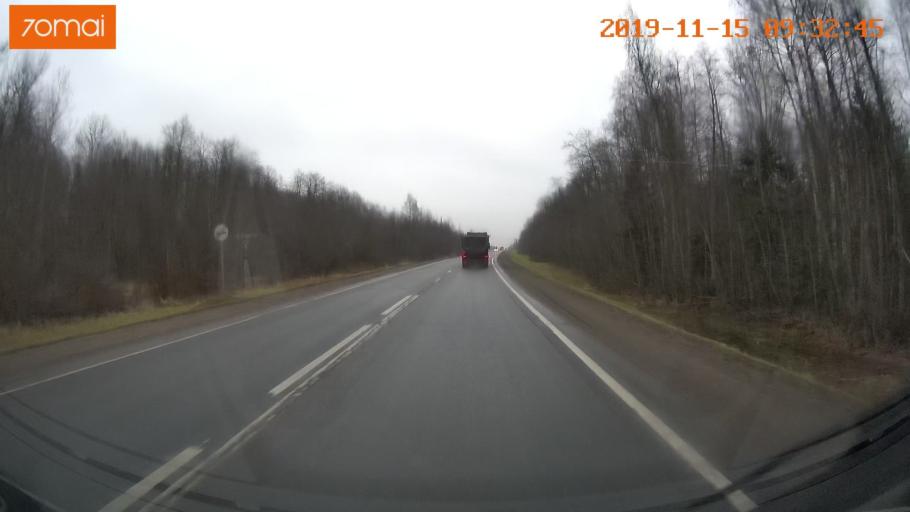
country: RU
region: Vologda
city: Sheksna
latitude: 59.2702
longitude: 38.3430
